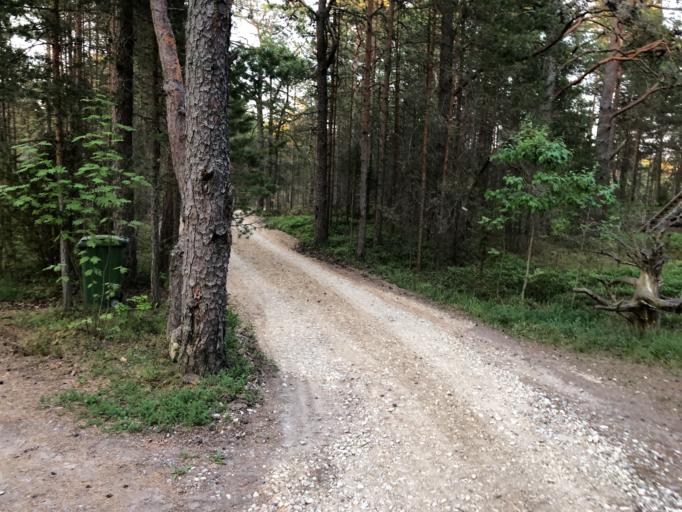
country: EE
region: Harju
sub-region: Paldiski linn
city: Paldiski
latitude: 59.3909
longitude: 24.2284
